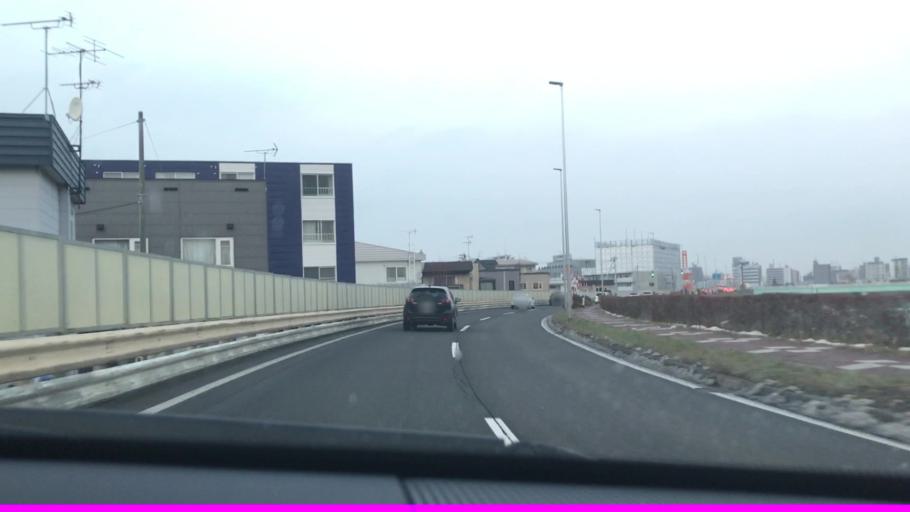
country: JP
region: Hokkaido
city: Sapporo
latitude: 43.0269
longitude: 141.3514
